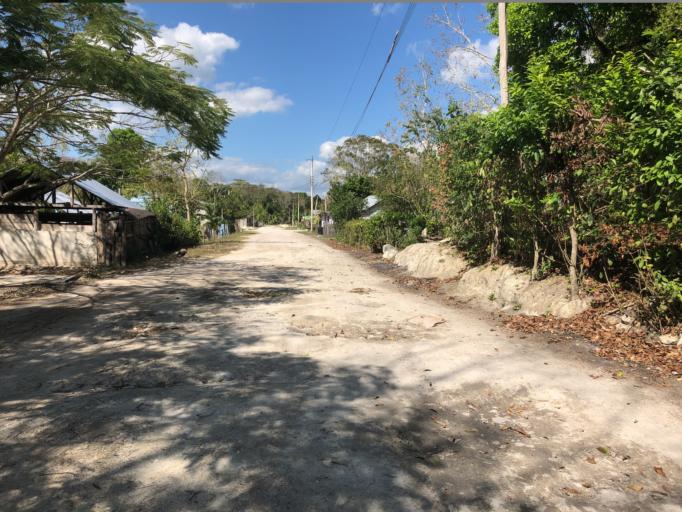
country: MX
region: Quintana Roo
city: Nicolas Bravo
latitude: 18.4512
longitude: -89.3063
